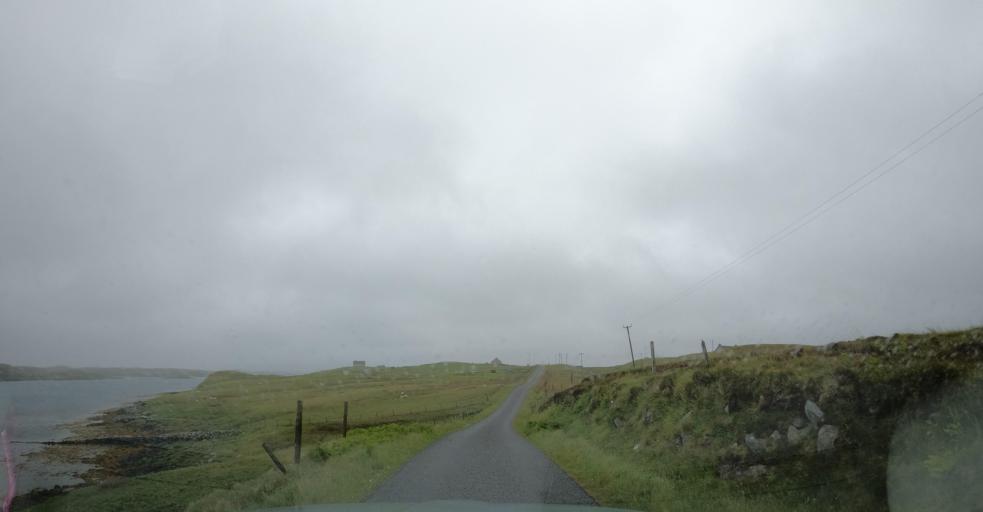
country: GB
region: Scotland
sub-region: Eilean Siar
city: Isle of North Uist
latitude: 57.5502
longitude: -7.2369
